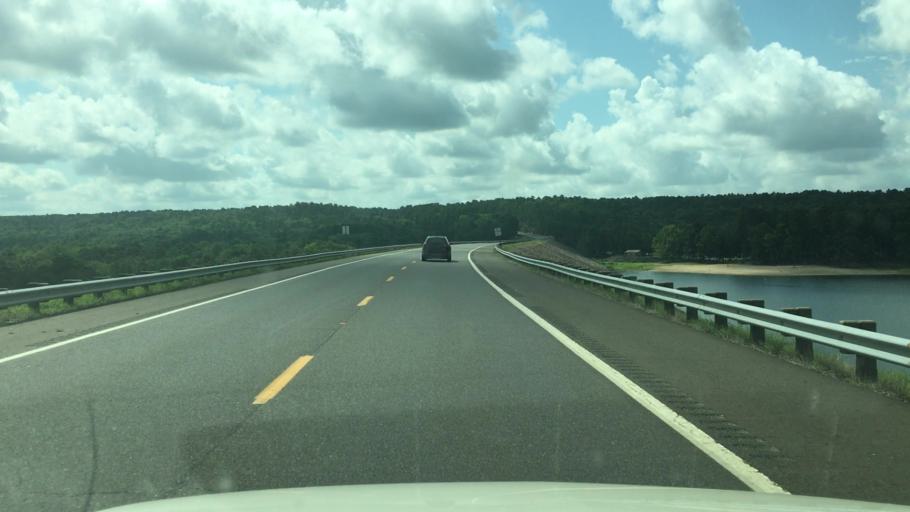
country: US
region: Arkansas
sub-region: Clark County
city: Arkadelphia
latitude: 34.2409
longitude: -93.1043
